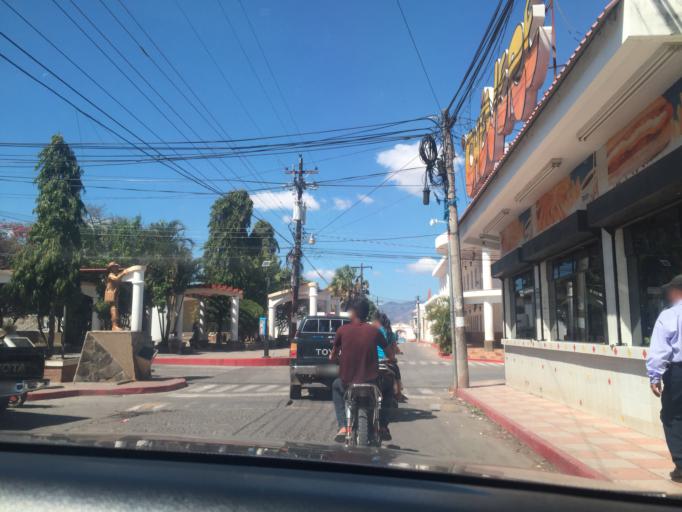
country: GT
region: Chiquimula
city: Ipala
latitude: 14.6196
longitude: -89.6237
